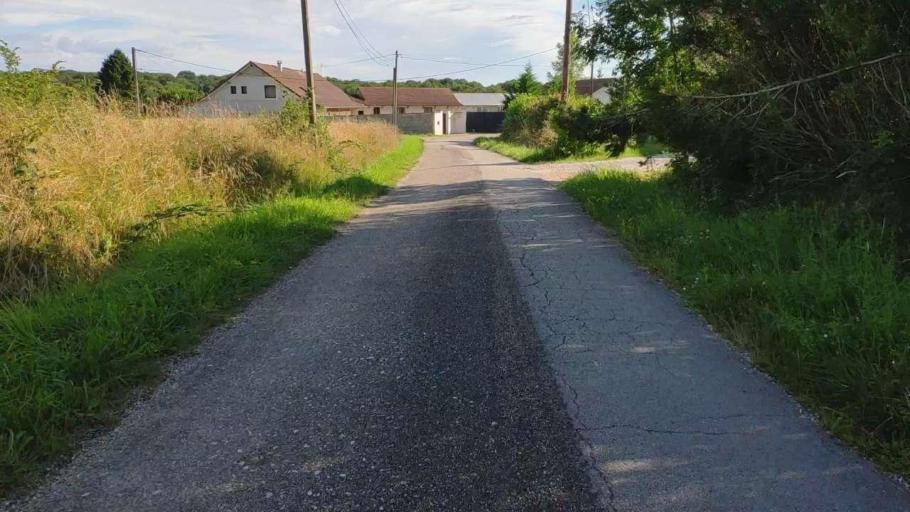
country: FR
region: Franche-Comte
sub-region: Departement du Jura
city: Bletterans
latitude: 46.8253
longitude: 5.5115
